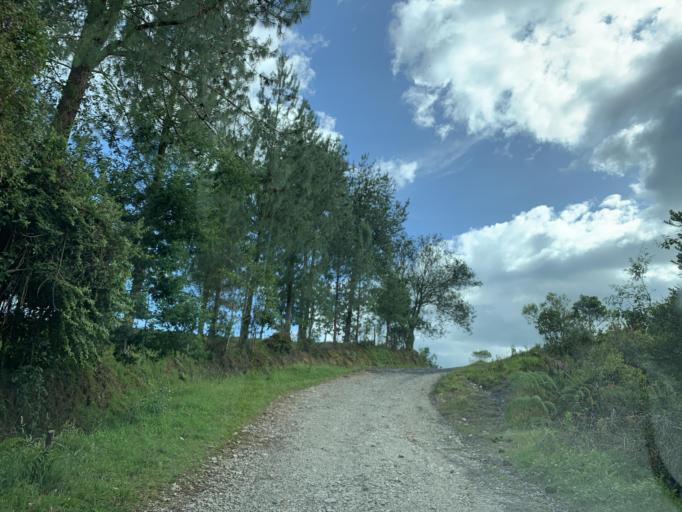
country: CO
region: Boyaca
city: Arcabuco
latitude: 5.7910
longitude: -73.4551
